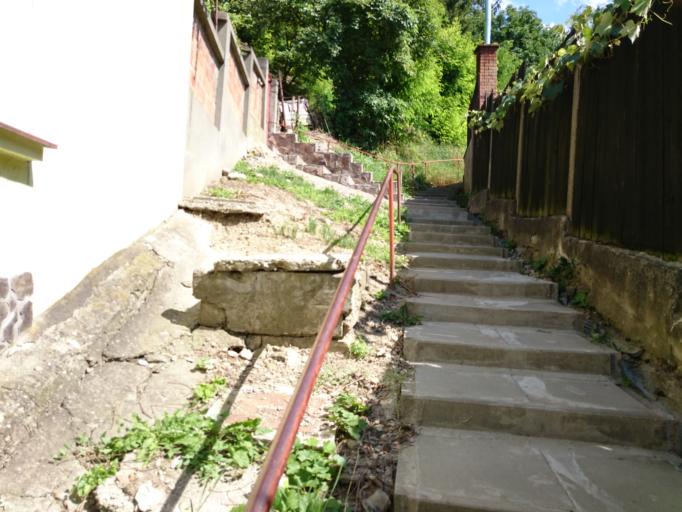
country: RO
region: Mures
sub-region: Municipiul Sighisoara
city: Sighisoara
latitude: 46.2163
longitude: 24.7954
